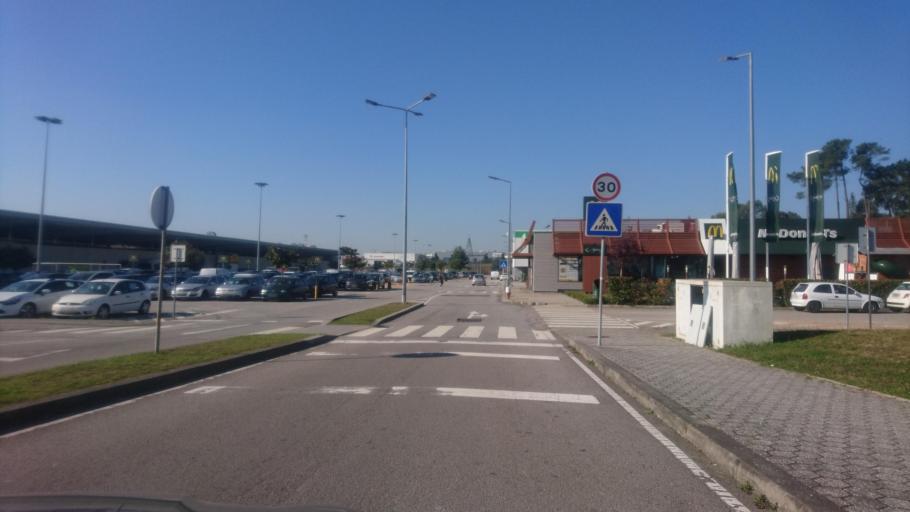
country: PT
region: Aveiro
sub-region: Santa Maria da Feira
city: Feira
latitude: 40.9224
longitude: -8.5641
